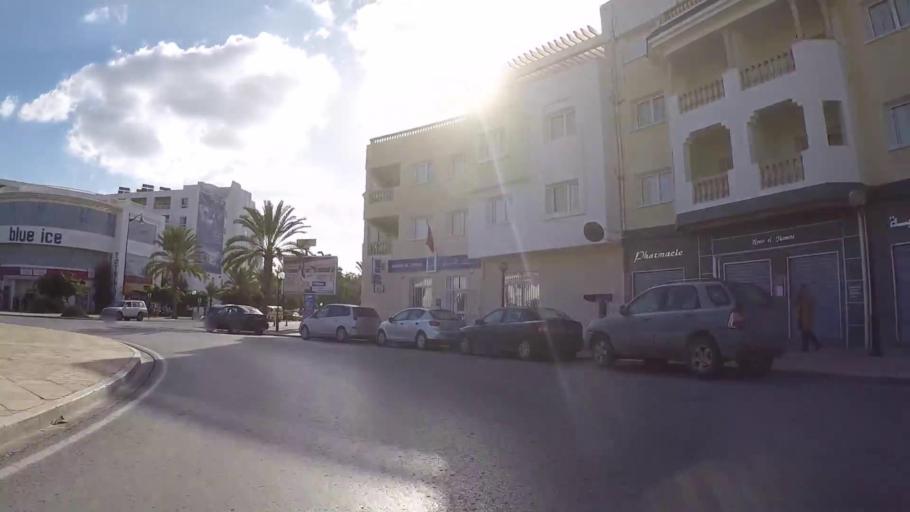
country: TN
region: Nabul
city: Al Hammamat
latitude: 36.3742
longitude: 10.5420
